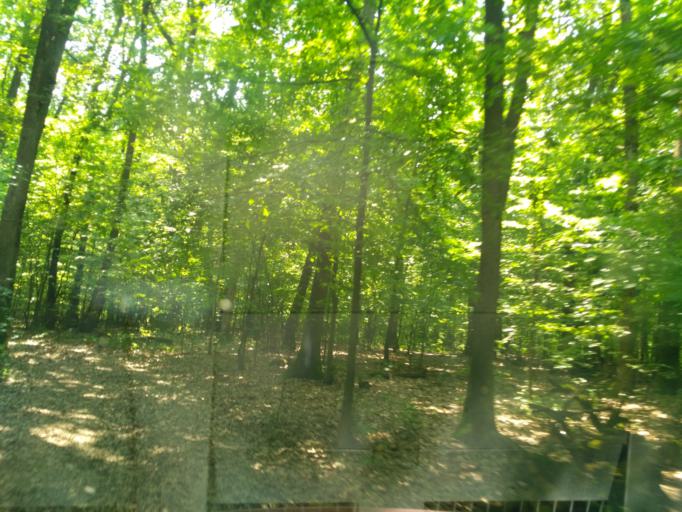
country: SK
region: Kosicky
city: Moldava nad Bodvou
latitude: 48.6414
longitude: 21.0403
